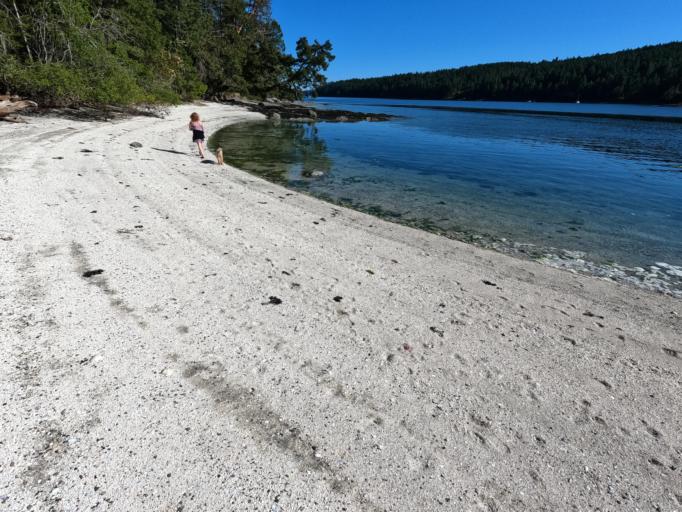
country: CA
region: British Columbia
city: North Saanich
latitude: 48.8944
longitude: -123.4074
